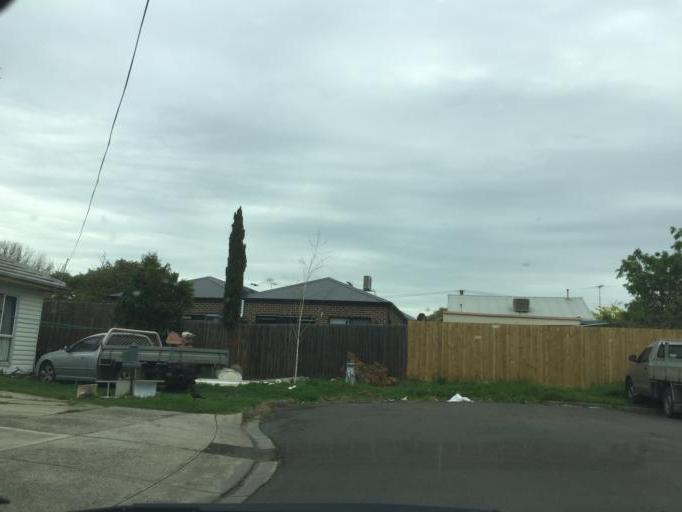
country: AU
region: Victoria
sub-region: Brimbank
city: Albion
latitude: -37.7812
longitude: 144.8395
